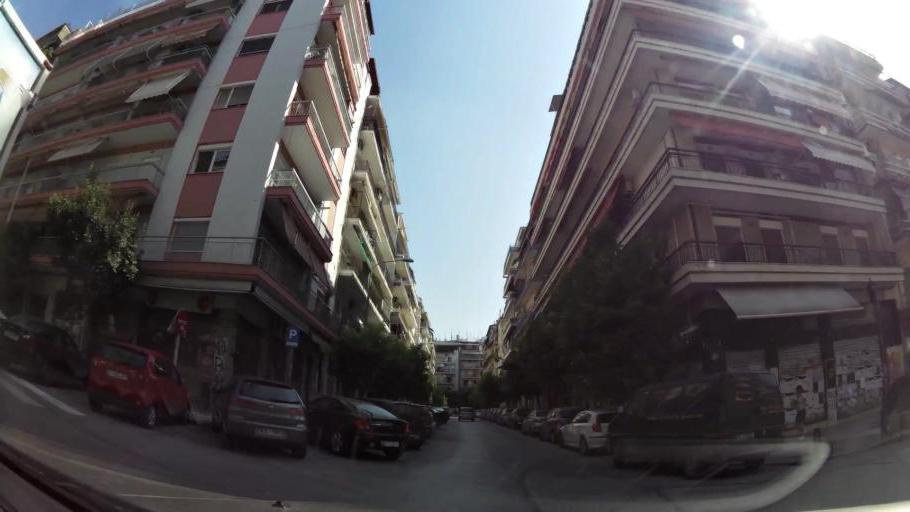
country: GR
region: Central Macedonia
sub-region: Nomos Thessalonikis
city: Agios Pavlos
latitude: 40.6345
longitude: 22.9520
